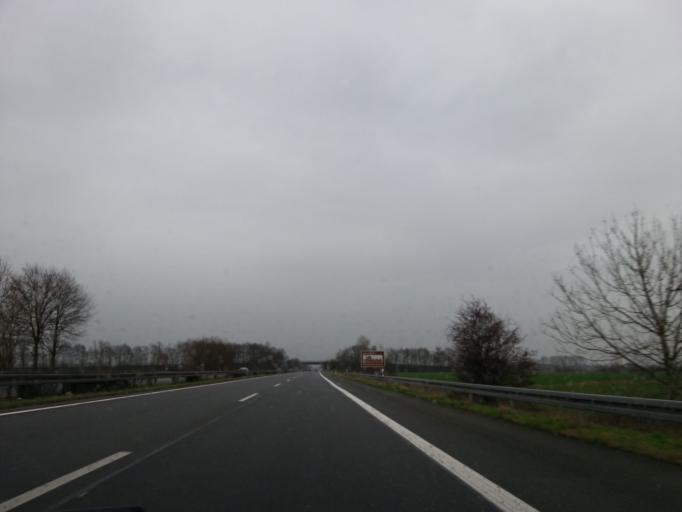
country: NL
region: Gelderland
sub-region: Oude IJsselstreek
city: Gendringen
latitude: 51.8407
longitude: 6.3471
